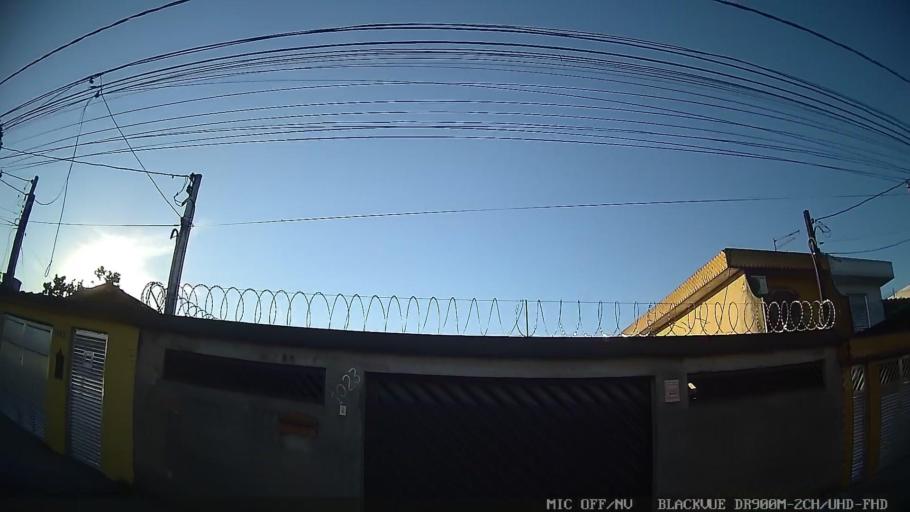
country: BR
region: Sao Paulo
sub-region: Guaruja
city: Guaruja
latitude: -23.9587
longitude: -46.2759
